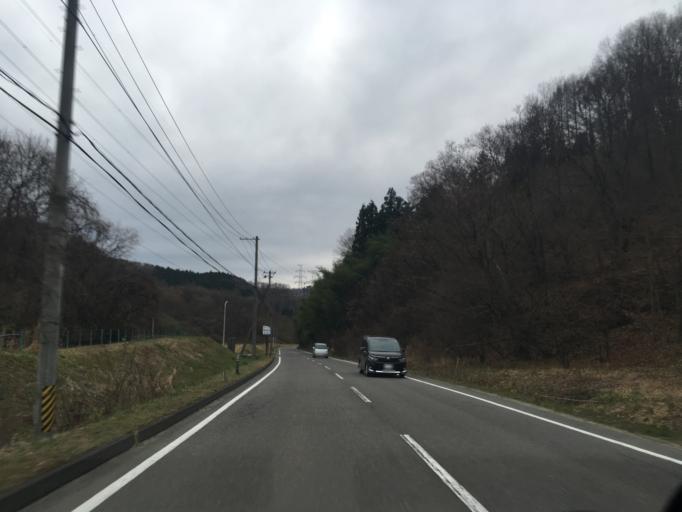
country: JP
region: Fukushima
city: Miharu
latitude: 37.3848
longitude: 140.4483
